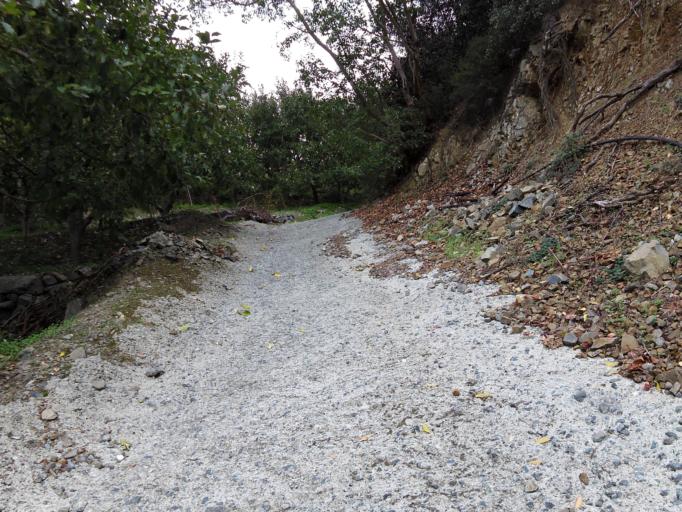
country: CY
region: Limassol
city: Kyperounta
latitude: 34.9316
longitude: 32.9377
